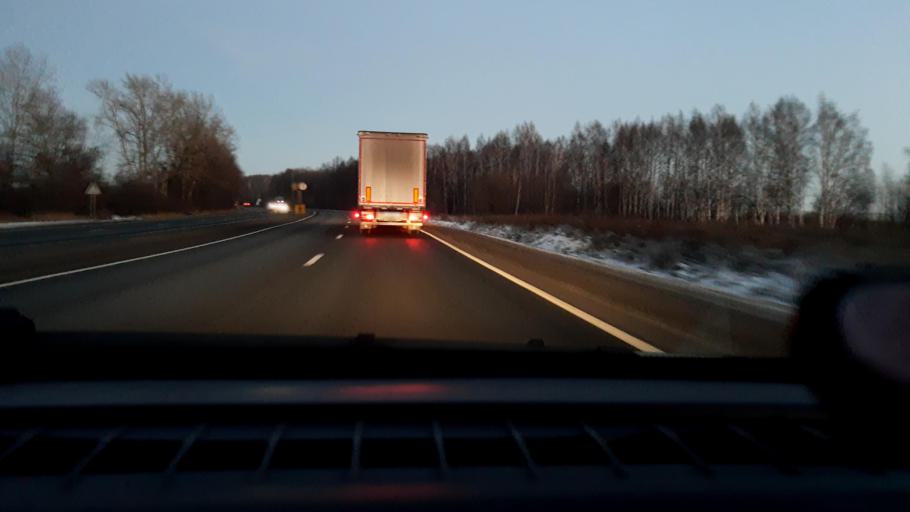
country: RU
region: Nizjnij Novgorod
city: Lyskovo
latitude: 56.0085
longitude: 44.9384
